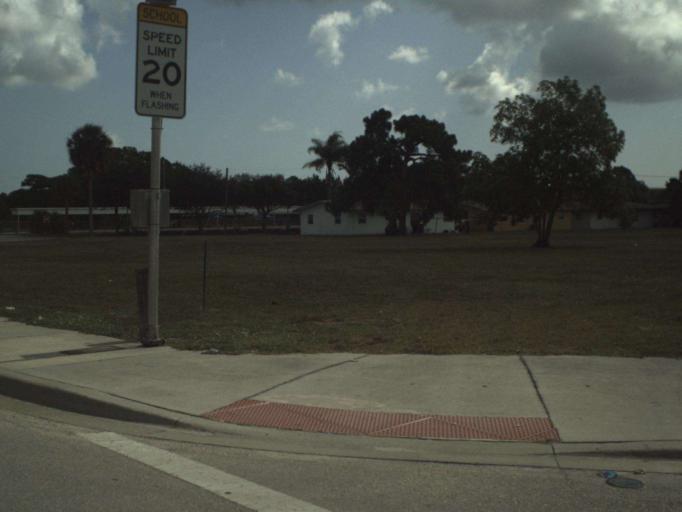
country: US
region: Florida
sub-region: Saint Lucie County
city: Fort Pierce North
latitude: 27.4648
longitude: -80.3497
